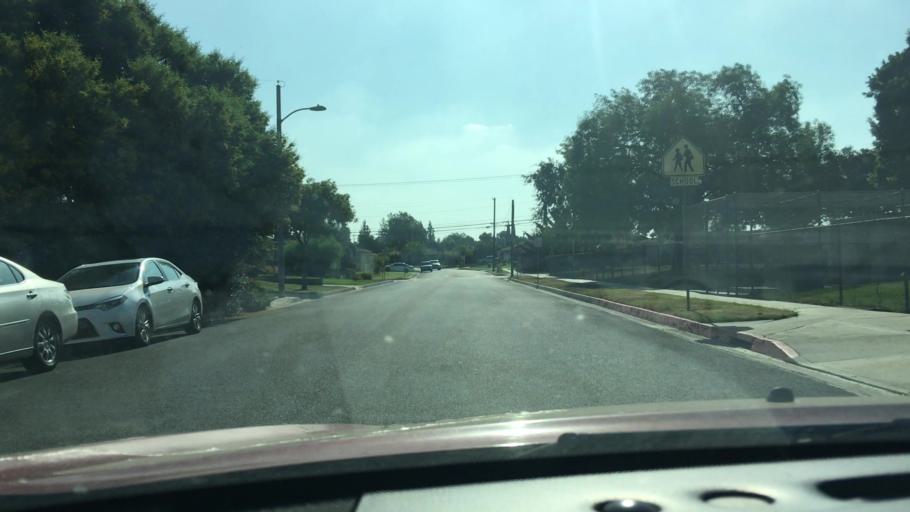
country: US
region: California
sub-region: Los Angeles County
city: La Mirada
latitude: 33.8943
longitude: -118.0127
